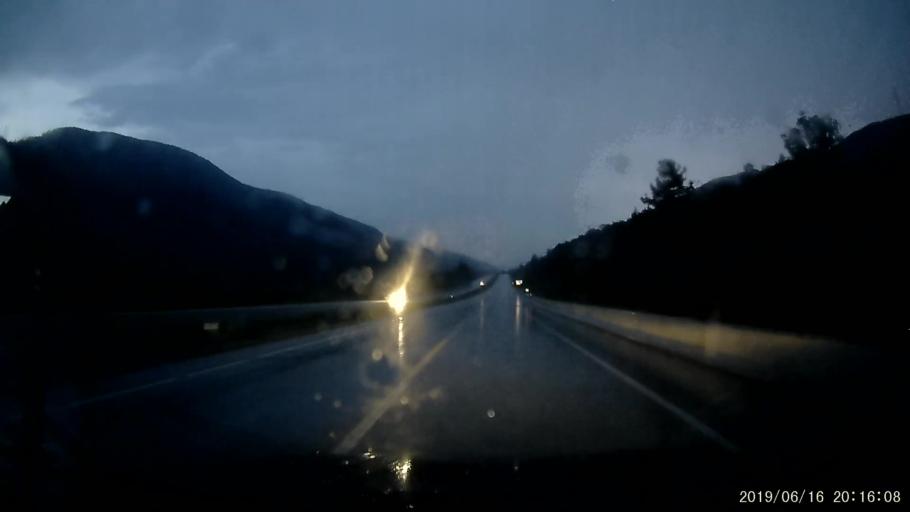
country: TR
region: Tokat
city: Resadiye
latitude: 40.3569
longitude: 37.4484
